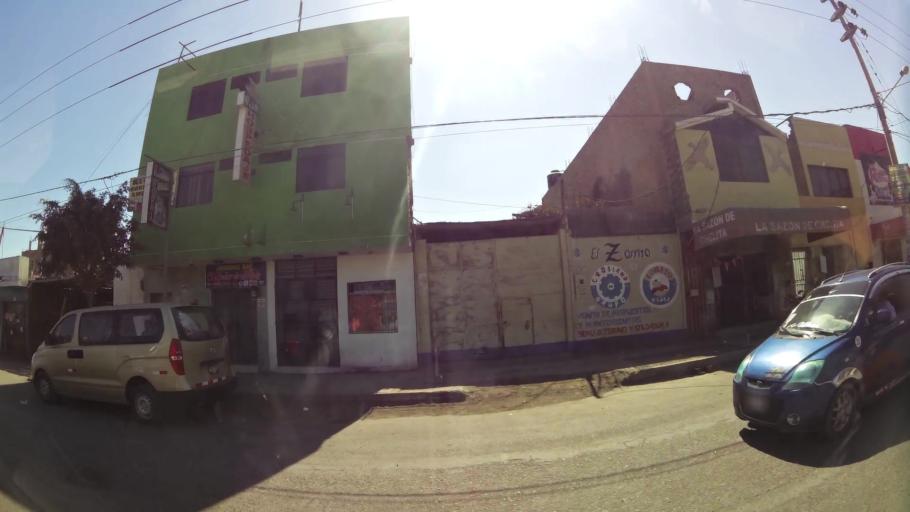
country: PE
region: Ica
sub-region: Provincia de Ica
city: La Tinguina
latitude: -14.0504
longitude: -75.7029
